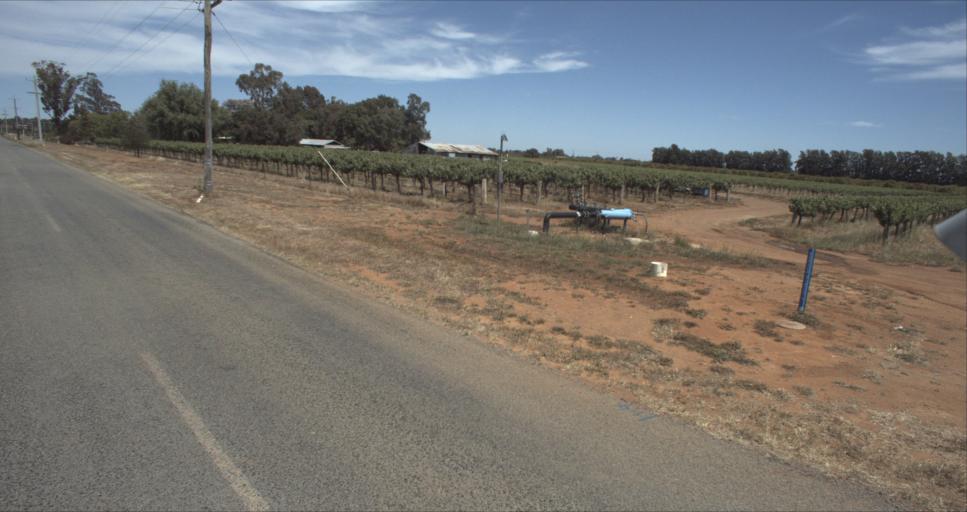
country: AU
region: New South Wales
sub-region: Leeton
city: Leeton
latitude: -34.5601
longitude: 146.4530
